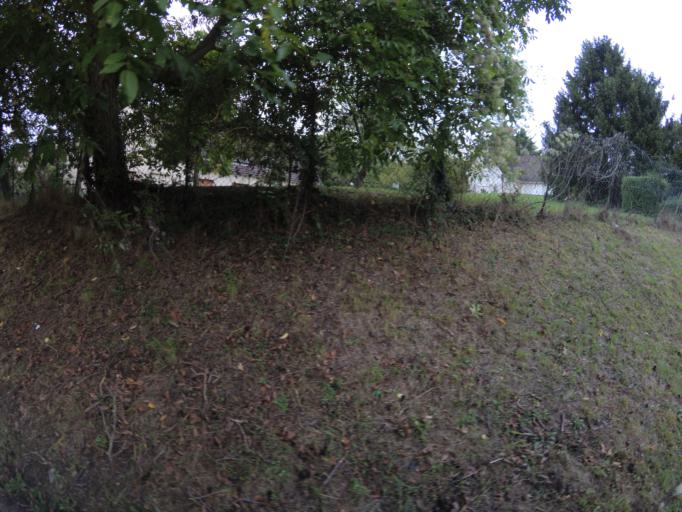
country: FR
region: Ile-de-France
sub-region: Departement de Seine-et-Marne
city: Gouvernes
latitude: 48.8616
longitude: 2.6909
